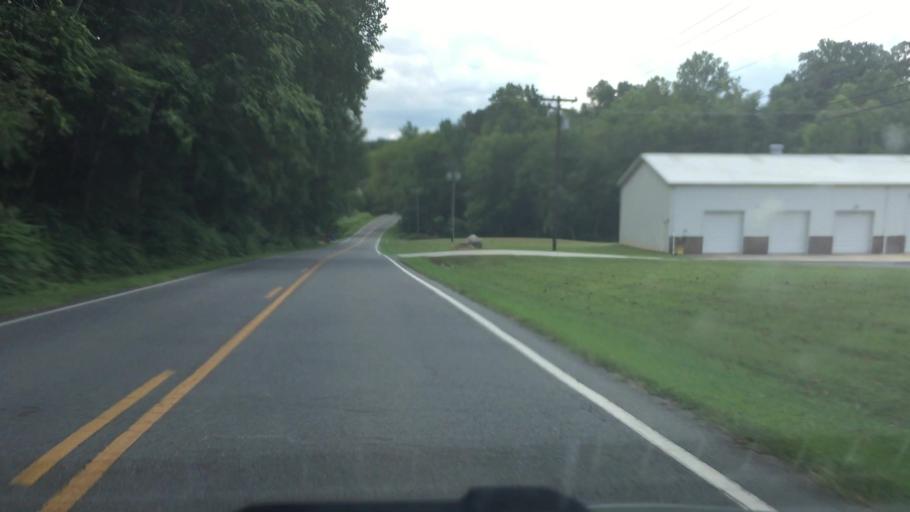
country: US
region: North Carolina
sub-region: Rowan County
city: Enochville
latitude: 35.4690
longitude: -80.7301
